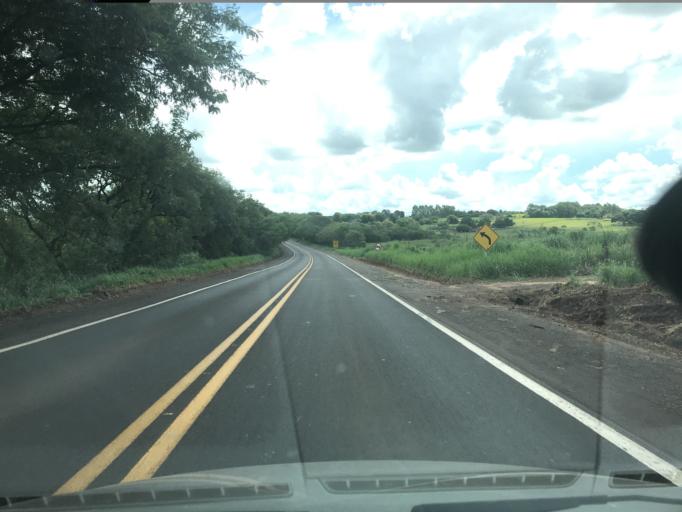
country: BR
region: Parana
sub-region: Cruzeiro Do Oeste
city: Cruzeiro do Oeste
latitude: -23.7891
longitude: -53.0313
